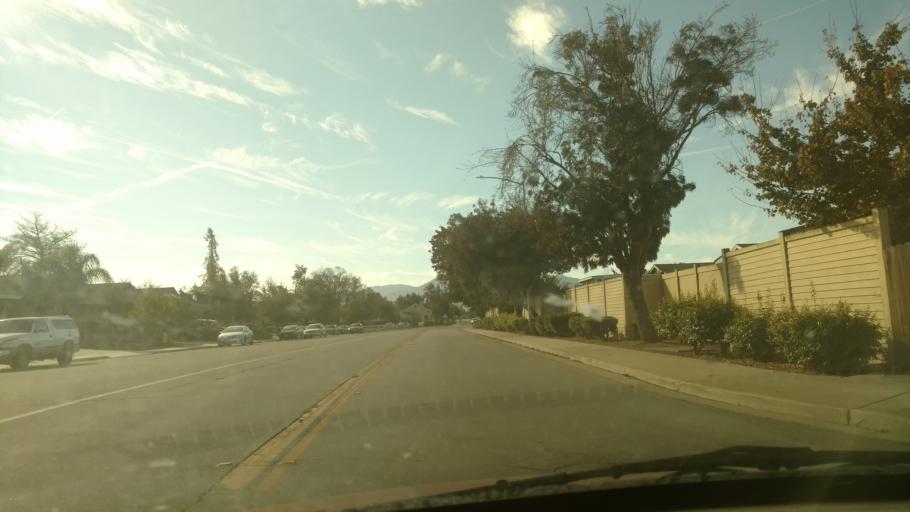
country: US
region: California
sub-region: San Benito County
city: Hollister
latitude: 36.8506
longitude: -121.4141
